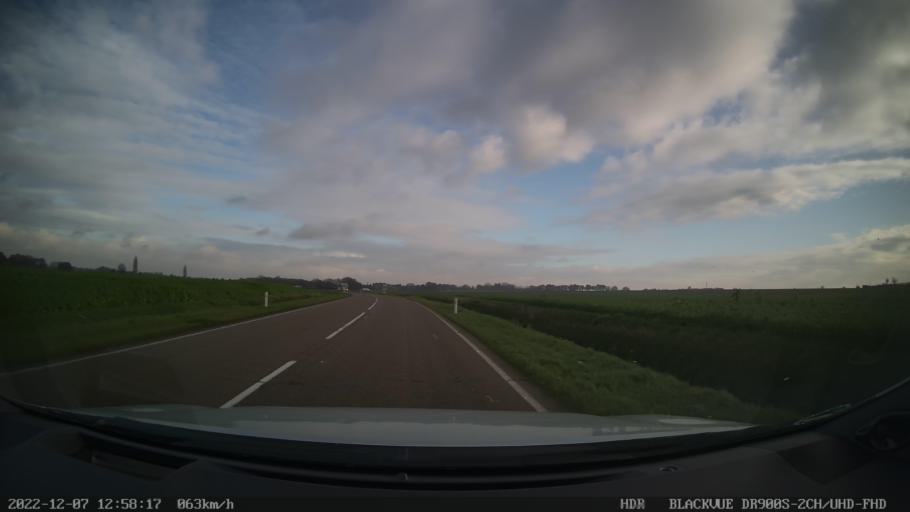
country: NL
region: Limburg
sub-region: Gemeente Beek
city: Beek
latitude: 50.9076
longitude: 5.7961
